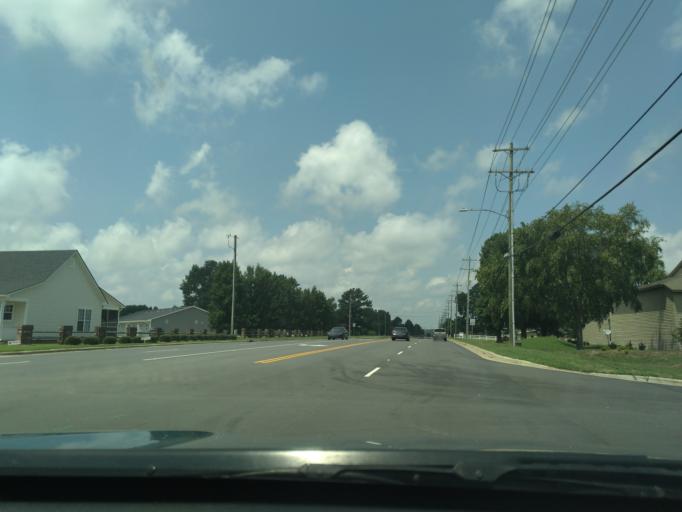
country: US
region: North Carolina
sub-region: Nash County
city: Rocky Mount
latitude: 35.9869
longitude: -77.8169
